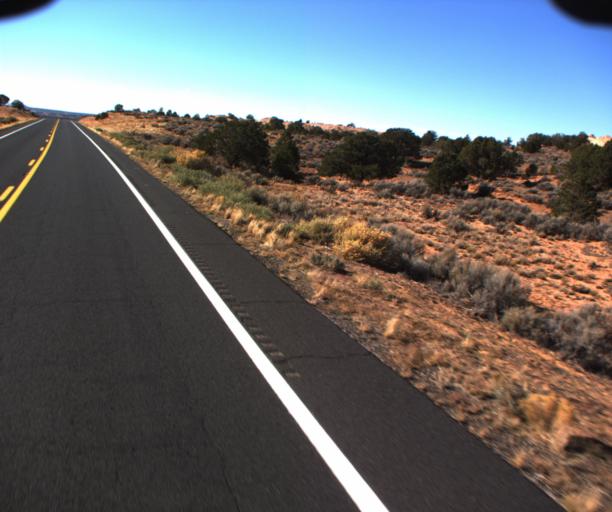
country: US
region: Arizona
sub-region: Coconino County
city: Kaibito
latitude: 36.5622
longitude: -110.7266
